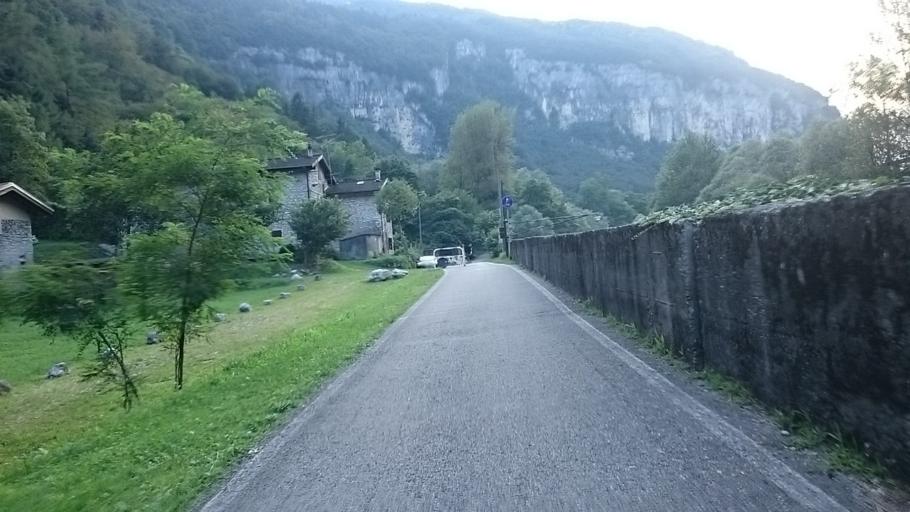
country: IT
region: Veneto
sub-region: Provincia di Vicenza
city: Enego
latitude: 45.9543
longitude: 11.7155
